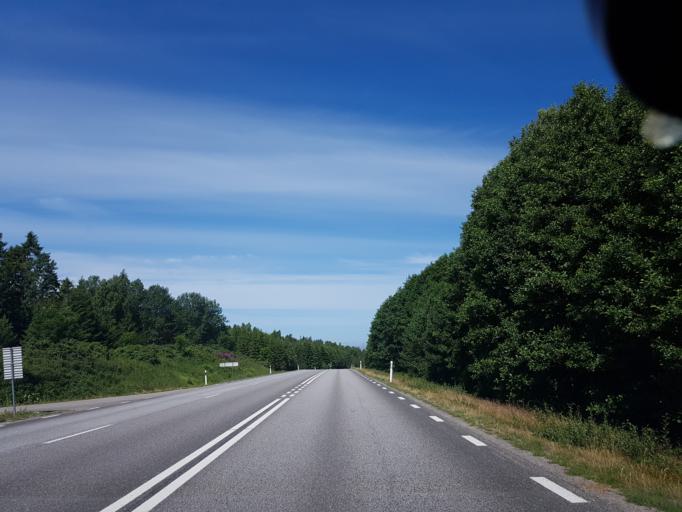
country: SE
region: Vaestra Goetaland
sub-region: Lysekils Kommun
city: Lysekil
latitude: 58.1603
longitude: 11.4962
